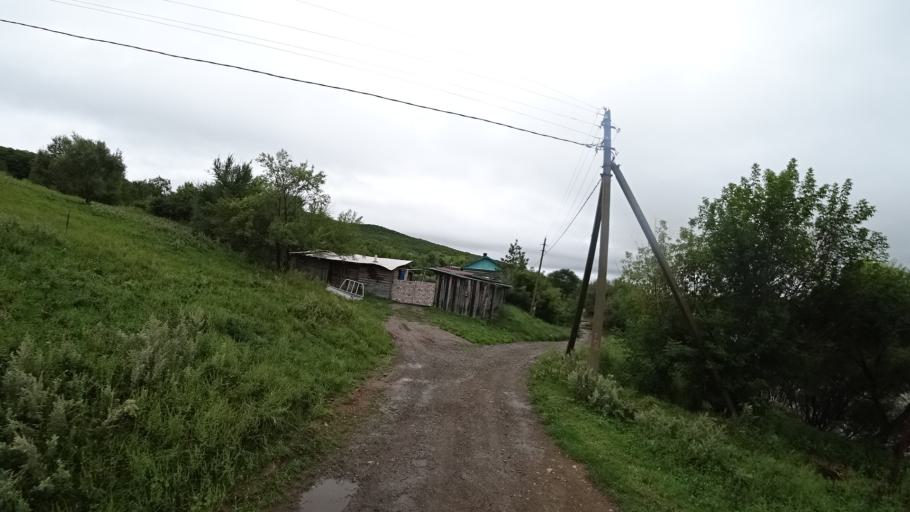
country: RU
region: Primorskiy
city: Monastyrishche
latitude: 44.2736
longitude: 132.4058
